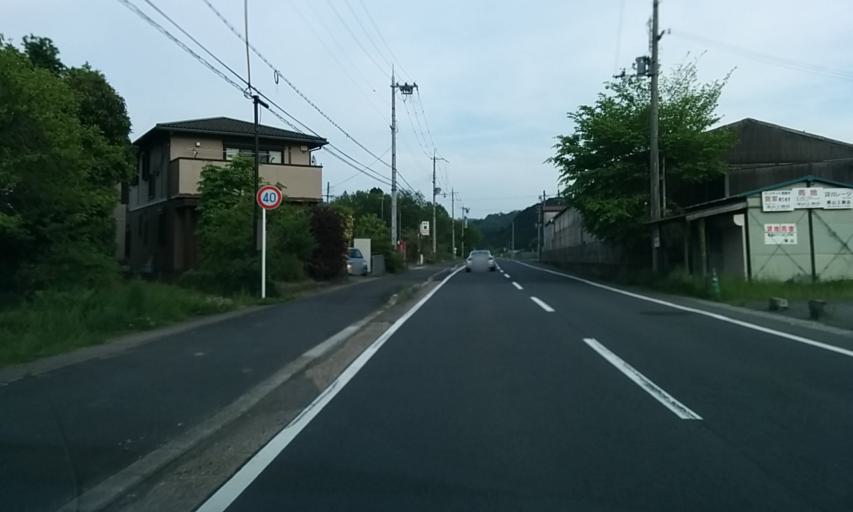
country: JP
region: Kyoto
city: Ayabe
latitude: 35.1639
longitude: 135.4040
